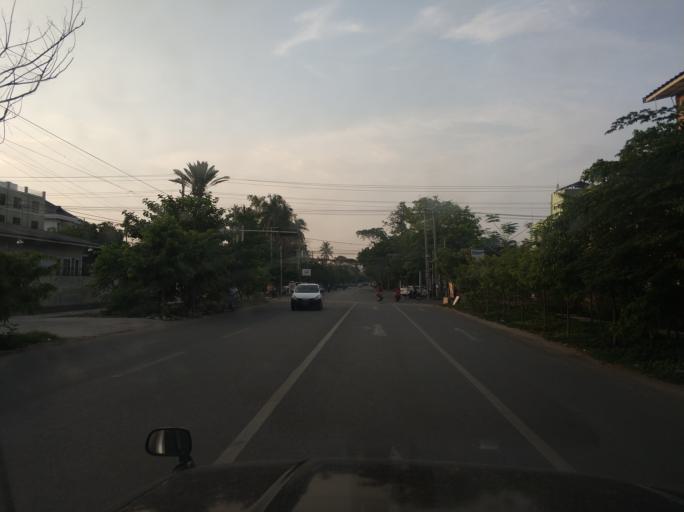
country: MM
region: Mandalay
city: Mandalay
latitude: 21.9722
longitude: 96.1060
